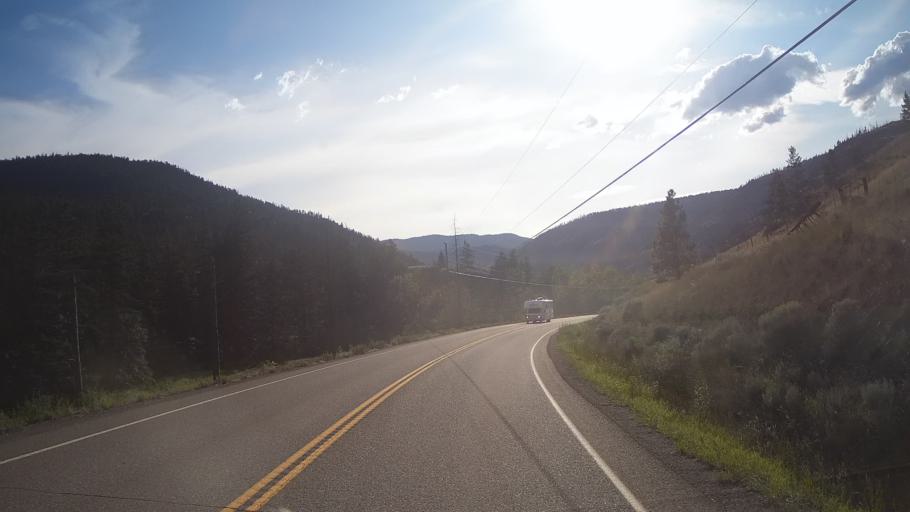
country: CA
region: British Columbia
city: Cache Creek
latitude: 50.8841
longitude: -121.4741
